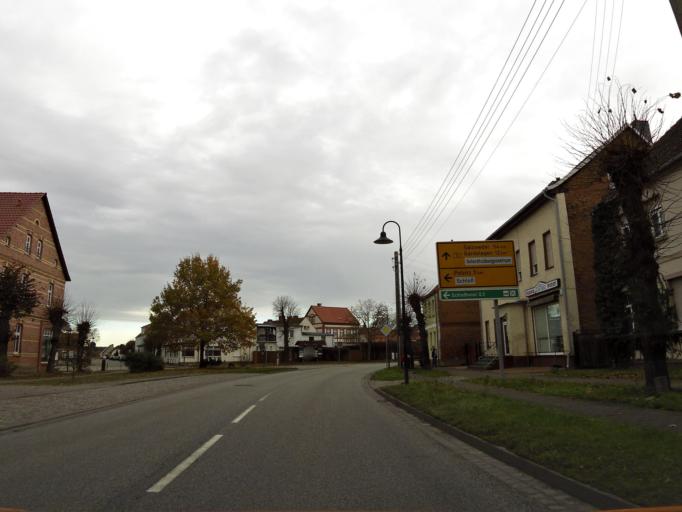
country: DE
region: Saxony-Anhalt
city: Letzlingen
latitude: 52.4461
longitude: 11.4861
